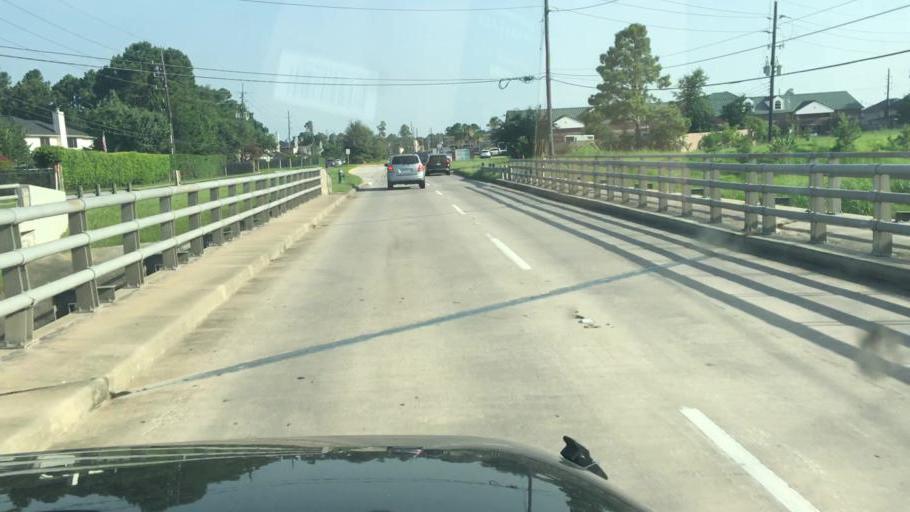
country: US
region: Texas
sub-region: Harris County
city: Atascocita
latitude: 29.9889
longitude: -95.1617
